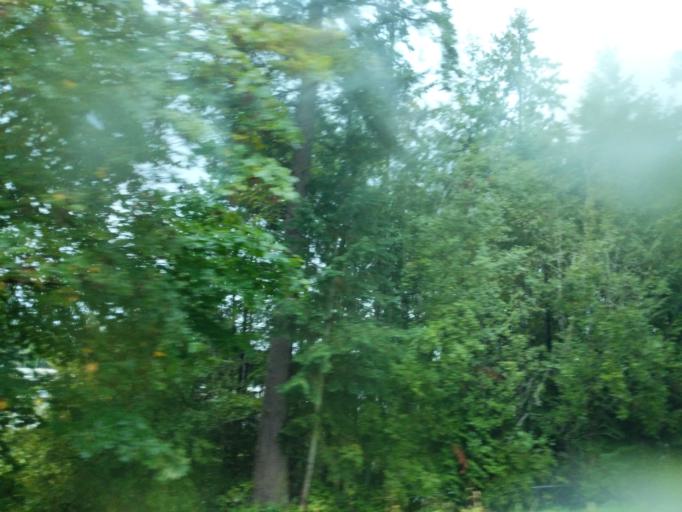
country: US
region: Washington
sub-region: King County
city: Bothell
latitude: 47.7805
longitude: -122.2072
